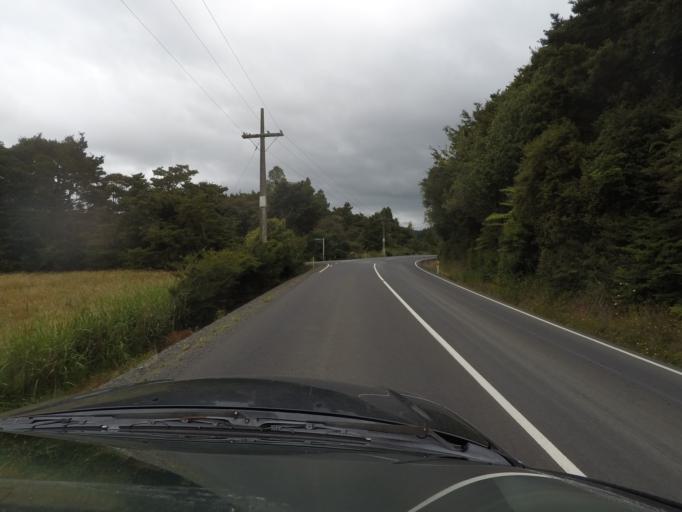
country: NZ
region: Auckland
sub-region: Auckland
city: Wellsford
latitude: -36.2856
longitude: 174.6129
